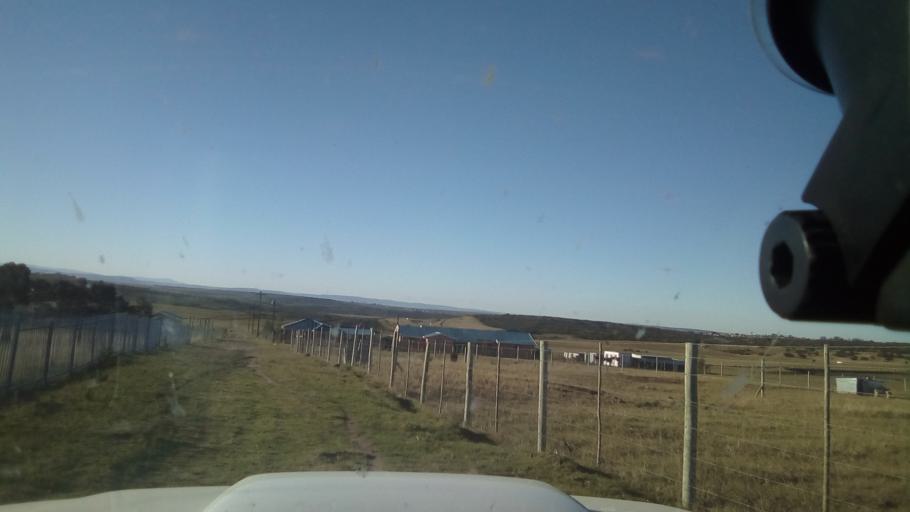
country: ZA
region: Eastern Cape
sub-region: Buffalo City Metropolitan Municipality
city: Bhisho
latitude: -32.9544
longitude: 27.2957
